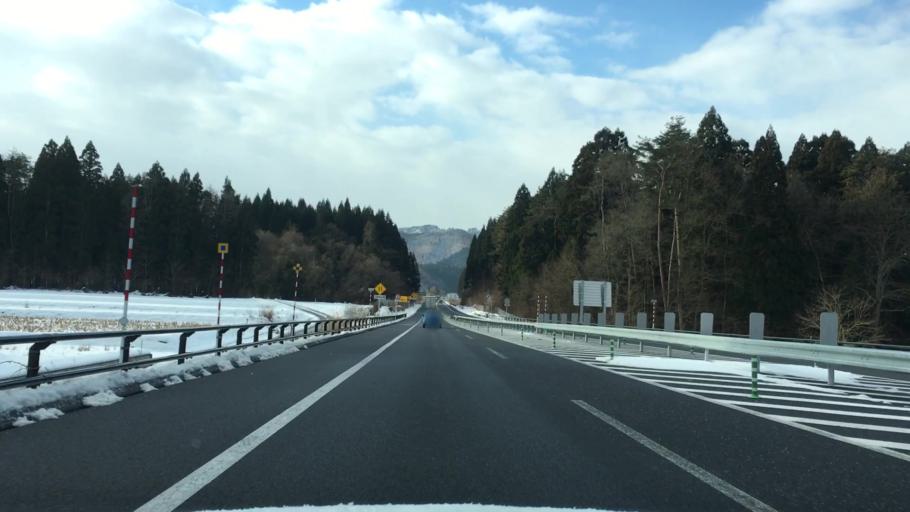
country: JP
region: Akita
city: Odate
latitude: 40.2450
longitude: 140.5106
